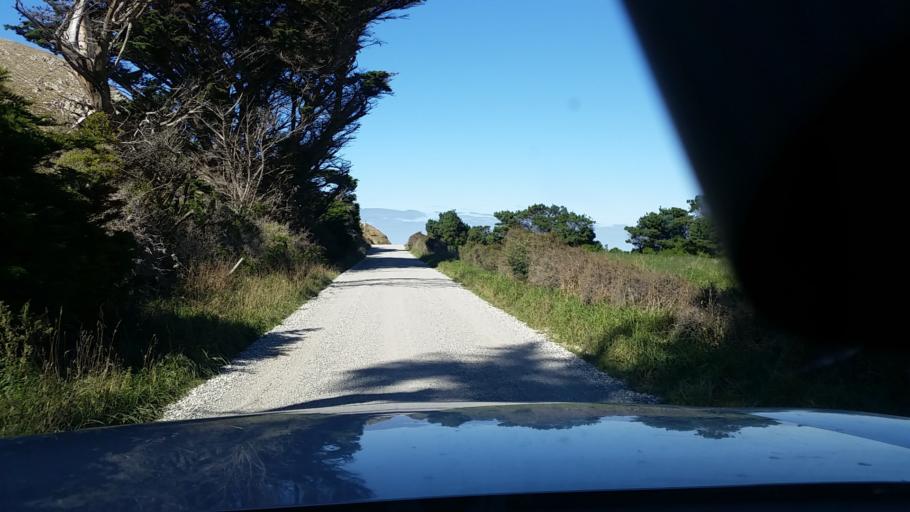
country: NZ
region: Marlborough
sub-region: Marlborough District
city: Blenheim
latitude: -41.8424
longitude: 174.1808
